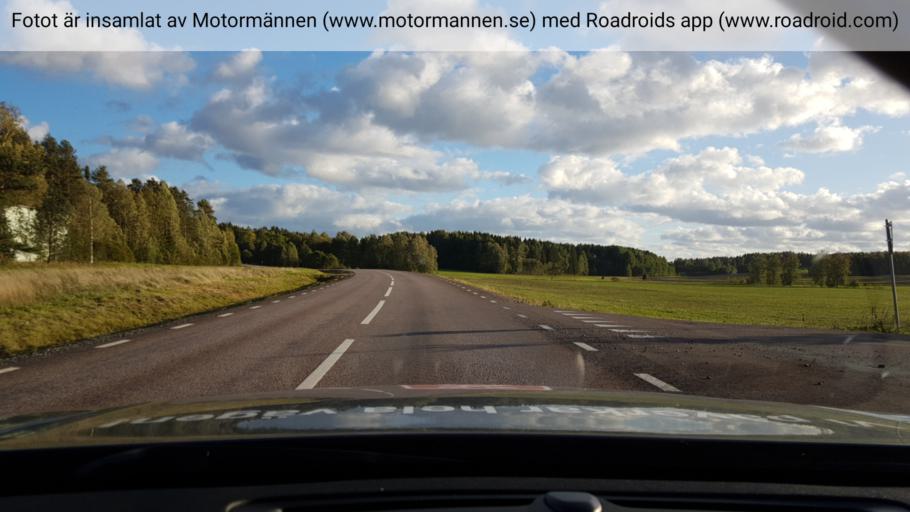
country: SE
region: Vaermland
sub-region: Karlstads Kommun
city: Molkom
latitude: 59.6183
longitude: 13.7290
